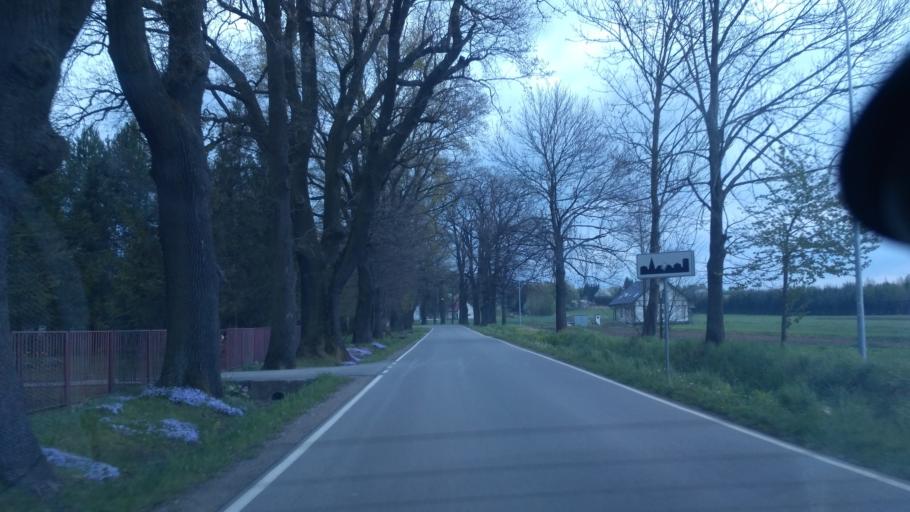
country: PL
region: Subcarpathian Voivodeship
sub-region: Powiat brzozowski
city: Turze Pole
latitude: 49.6484
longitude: 21.9933
